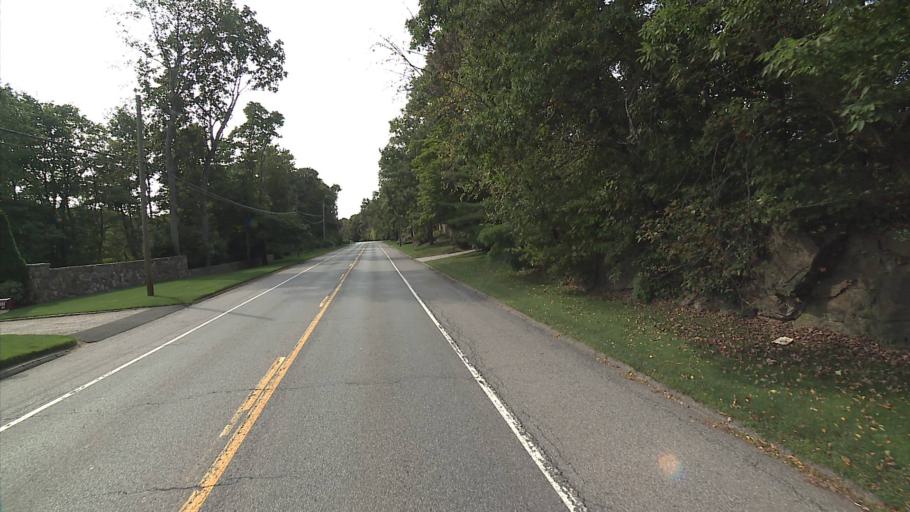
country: US
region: Connecticut
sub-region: Fairfield County
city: New Canaan
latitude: 41.1897
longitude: -73.5059
